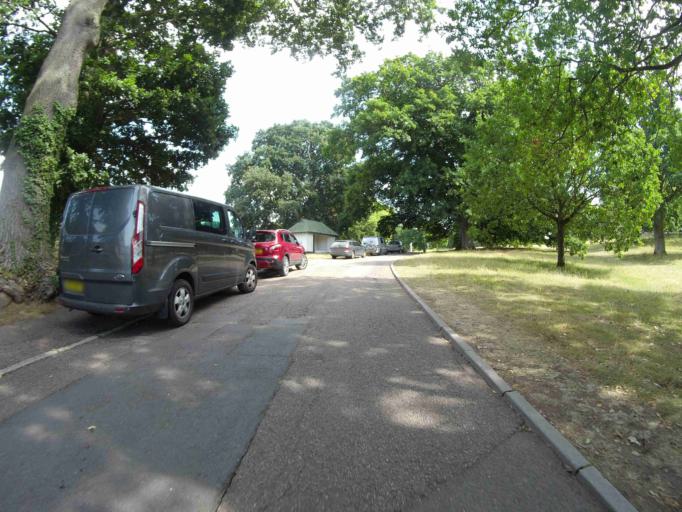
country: GB
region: England
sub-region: Devon
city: Exmouth
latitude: 50.6249
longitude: -3.4062
